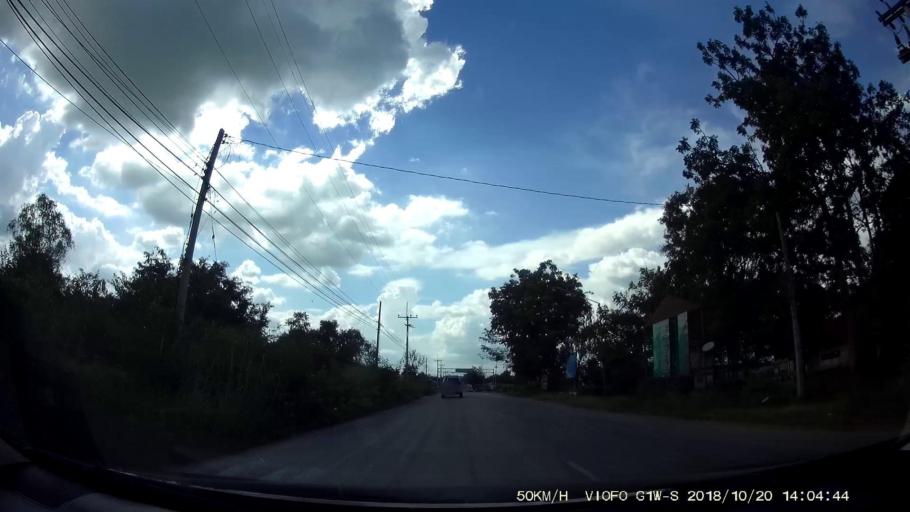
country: TH
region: Khon Kaen
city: Chum Phae
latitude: 16.4899
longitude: 102.1142
